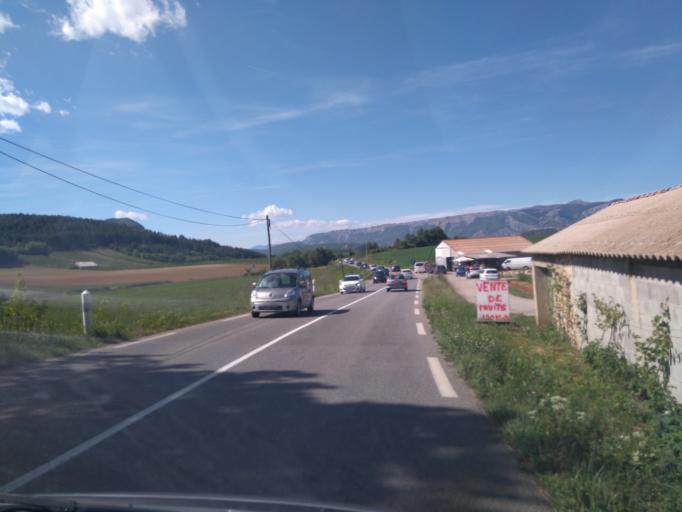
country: FR
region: Provence-Alpes-Cote d'Azur
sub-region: Departement des Hautes-Alpes
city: Laragne-Monteglin
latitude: 44.2805
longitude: 5.8482
